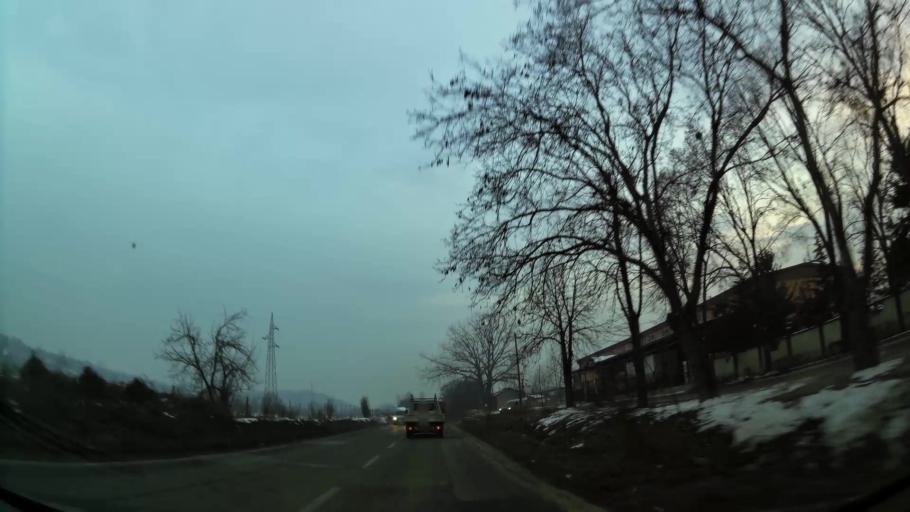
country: MK
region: Suto Orizari
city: Suto Orizare
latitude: 42.0223
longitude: 21.4096
